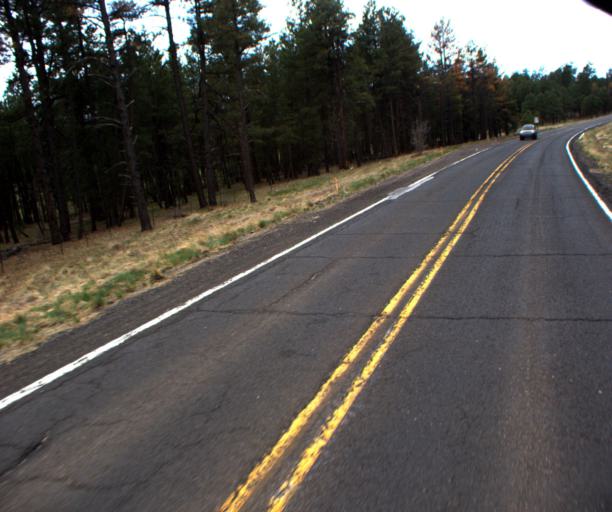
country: US
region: Arizona
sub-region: Coconino County
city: Kachina Village
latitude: 35.1234
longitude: -111.6963
